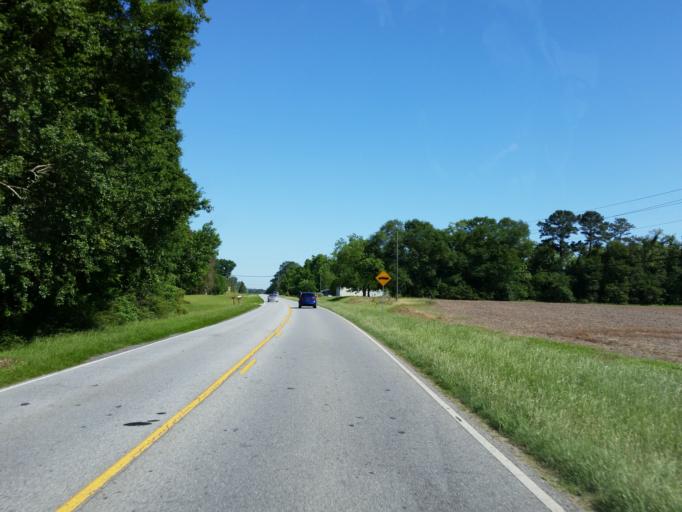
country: US
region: Georgia
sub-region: Lowndes County
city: Remerton
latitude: 30.9073
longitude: -83.3430
